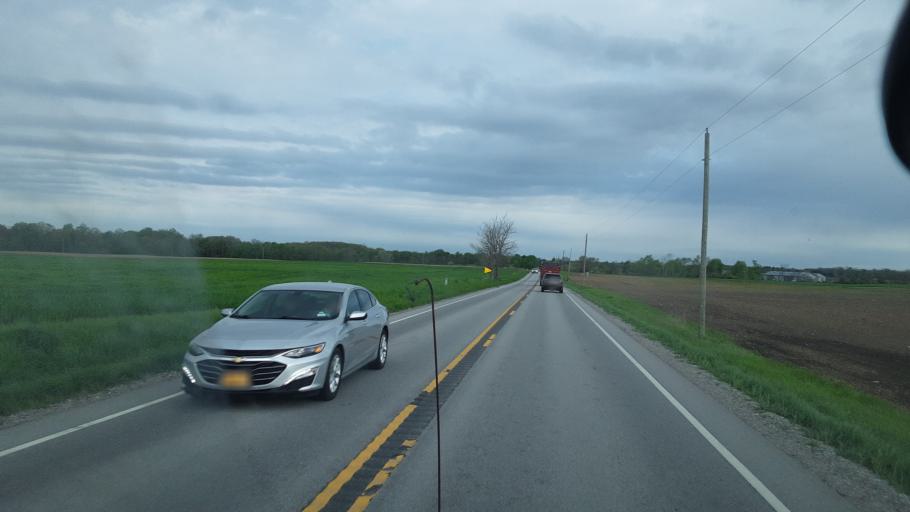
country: US
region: Indiana
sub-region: Whitley County
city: Tri-Lakes
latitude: 41.2752
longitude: -85.4142
